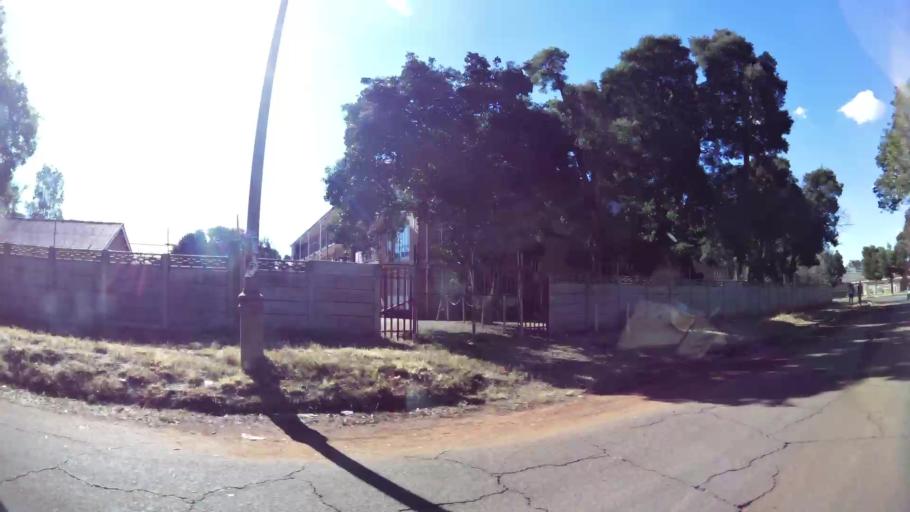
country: ZA
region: Gauteng
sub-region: West Rand District Municipality
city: Carletonville
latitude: -26.3605
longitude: 27.3966
